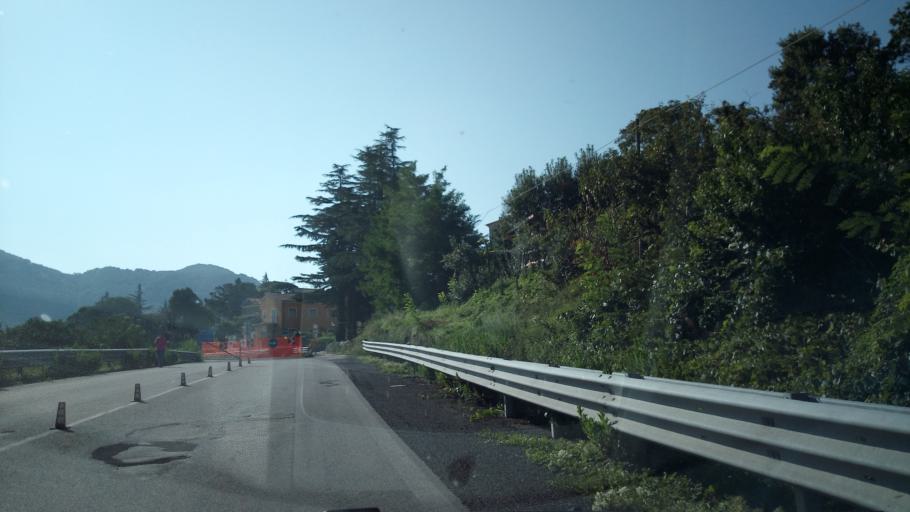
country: IT
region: Campania
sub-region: Provincia di Avellino
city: Parolise
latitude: 40.9327
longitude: 14.8800
